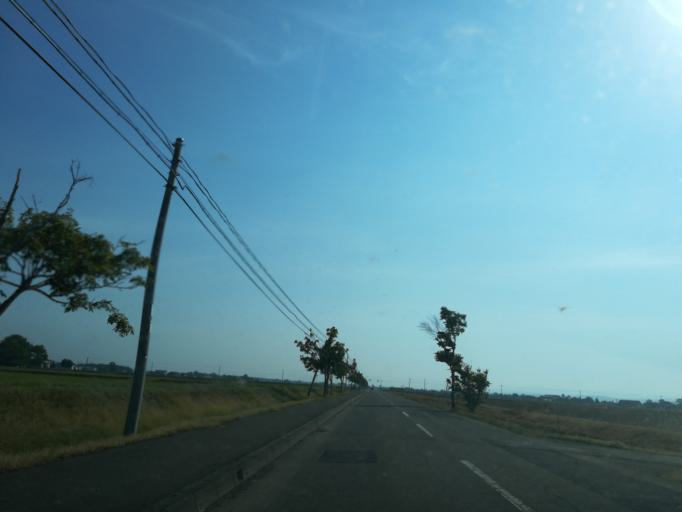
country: JP
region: Hokkaido
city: Iwamizawa
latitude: 43.1572
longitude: 141.6790
